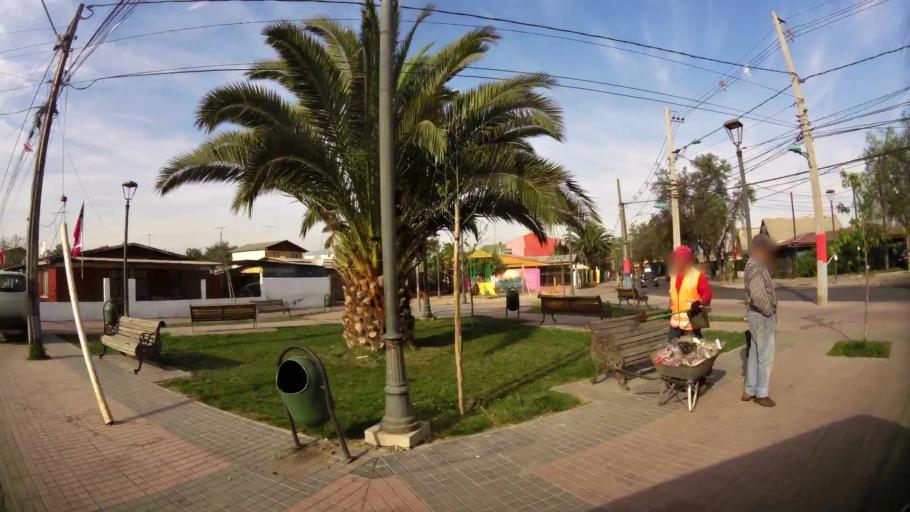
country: CL
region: Santiago Metropolitan
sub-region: Provincia de Talagante
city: Talagante
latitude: -33.6674
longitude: -70.9336
